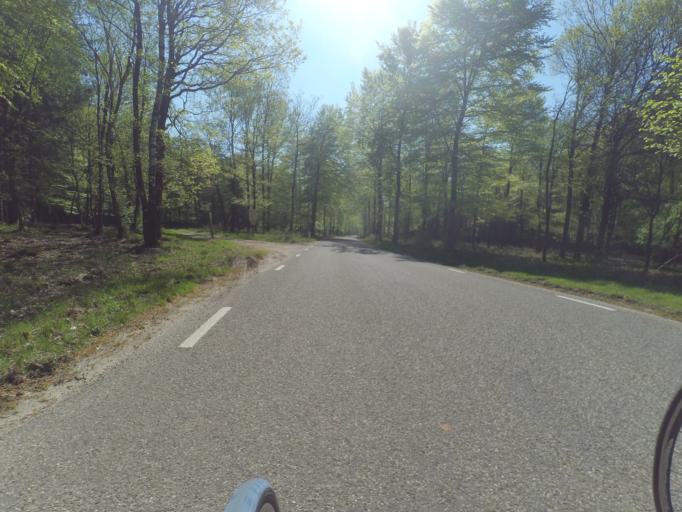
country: NL
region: Gelderland
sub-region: Gemeente Apeldoorn
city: Uddel
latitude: 52.2312
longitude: 5.8651
